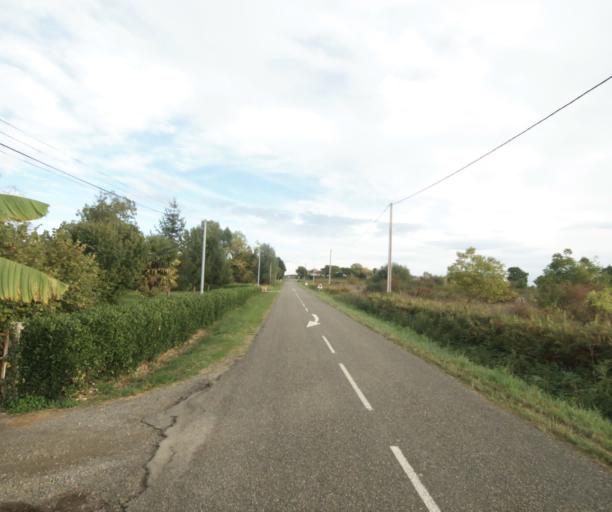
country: FR
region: Midi-Pyrenees
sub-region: Departement du Gers
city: Le Houga
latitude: 43.8569
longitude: -0.1433
